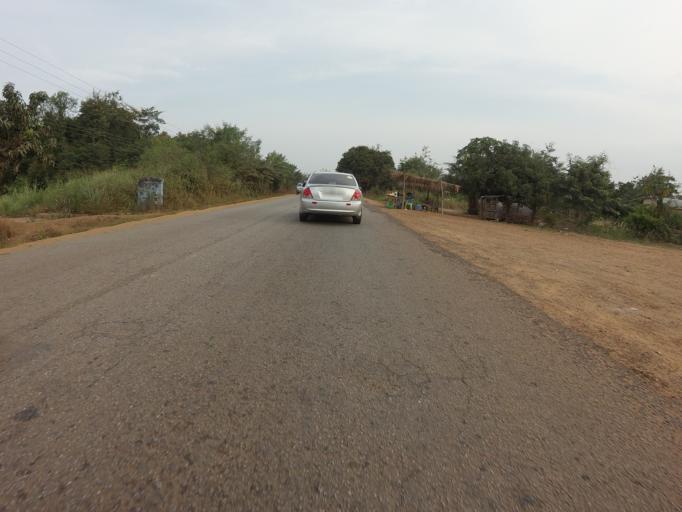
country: GH
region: Volta
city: Ho
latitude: 6.3810
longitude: 0.1865
